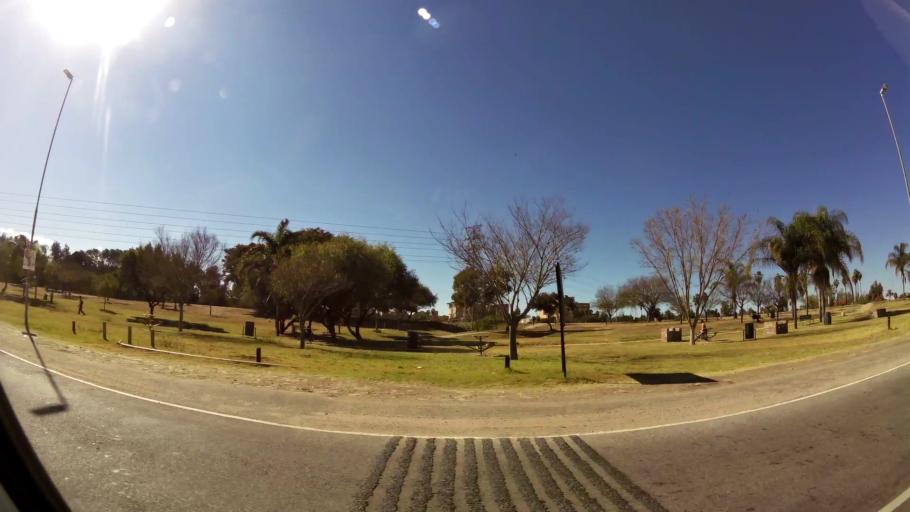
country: ZA
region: Limpopo
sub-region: Capricorn District Municipality
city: Polokwane
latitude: -23.9127
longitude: 29.4447
